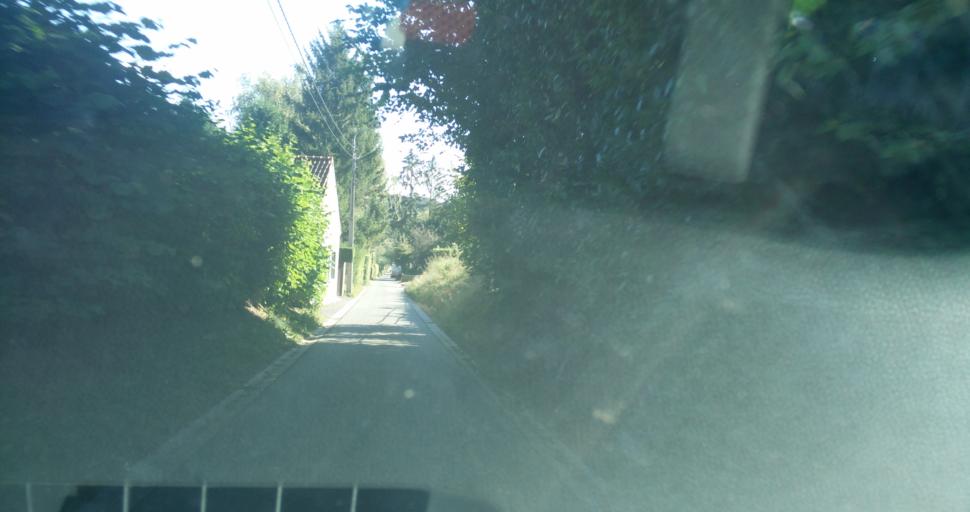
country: BE
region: Flanders
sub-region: Provincie Vlaams-Brabant
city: Halle
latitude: 50.7249
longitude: 4.2772
